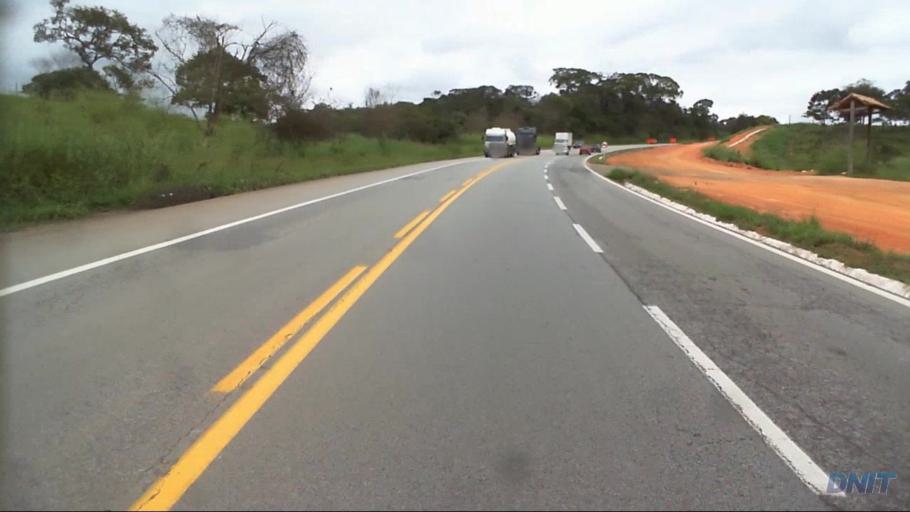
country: BR
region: Minas Gerais
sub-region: Barao De Cocais
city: Barao de Cocais
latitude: -19.7586
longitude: -43.4693
